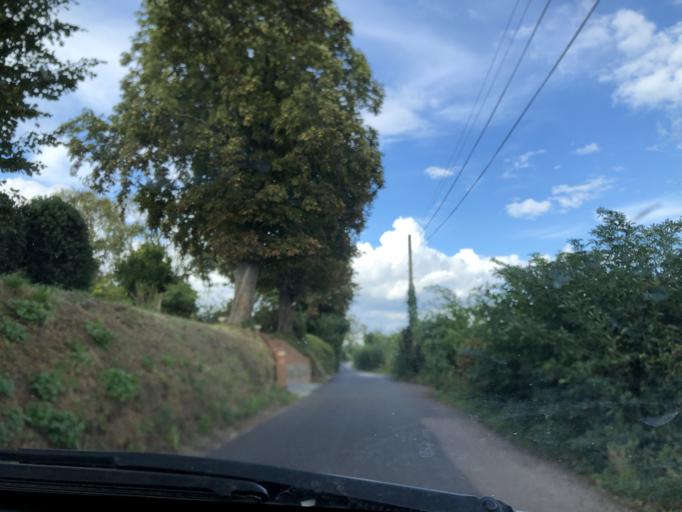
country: GB
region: England
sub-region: Kent
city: Eynsford
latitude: 51.3738
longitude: 0.2121
